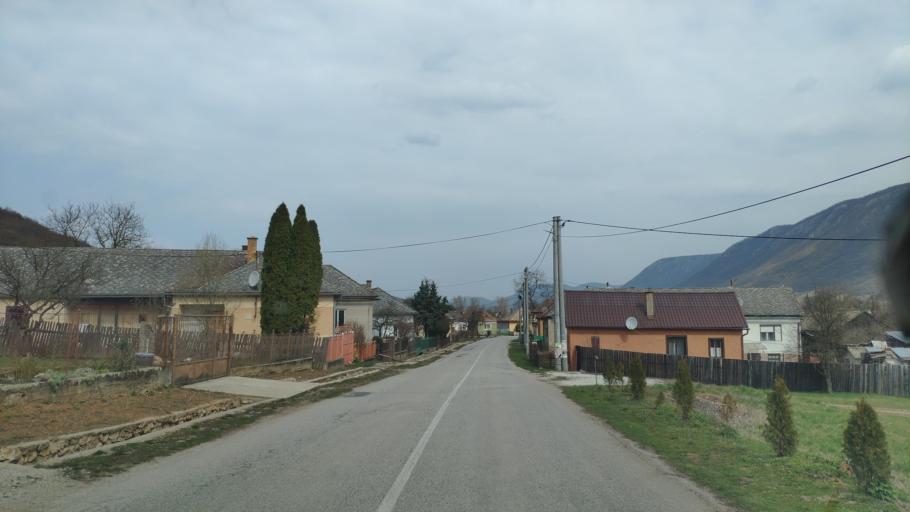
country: SK
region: Kosicky
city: Roznava
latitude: 48.5896
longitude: 20.3824
